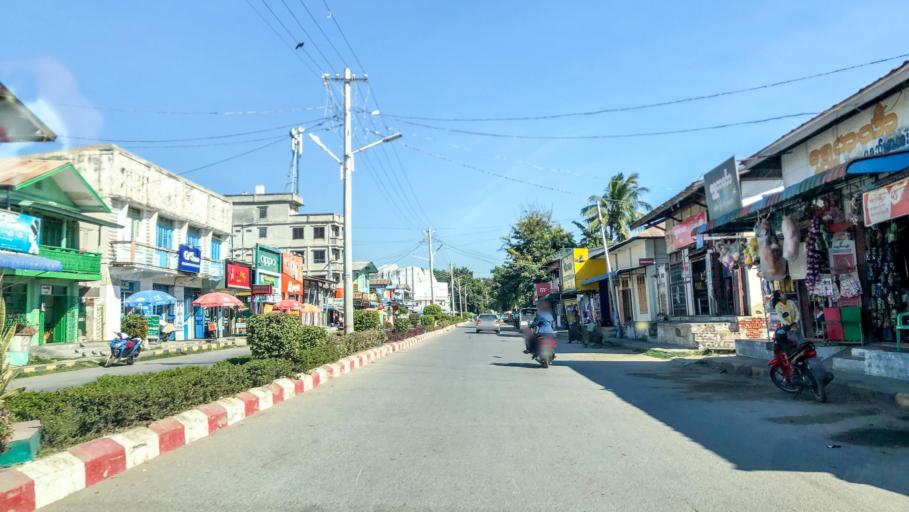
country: MM
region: Sagain
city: Sagaing
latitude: 21.8798
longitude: 95.9821
